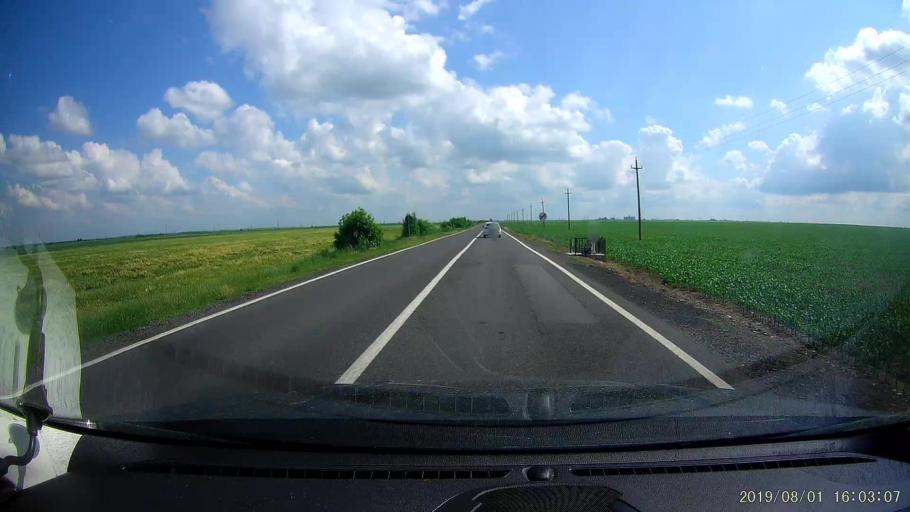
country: RO
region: Calarasi
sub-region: Comuna Dragalina
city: Drajna Noua
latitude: 44.4782
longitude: 27.3855
